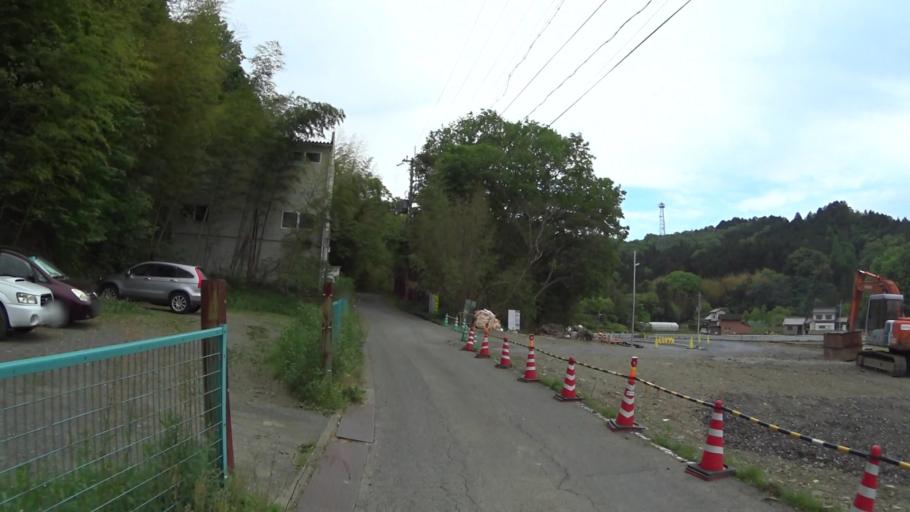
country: JP
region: Kyoto
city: Kameoka
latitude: 35.0646
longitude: 135.5336
